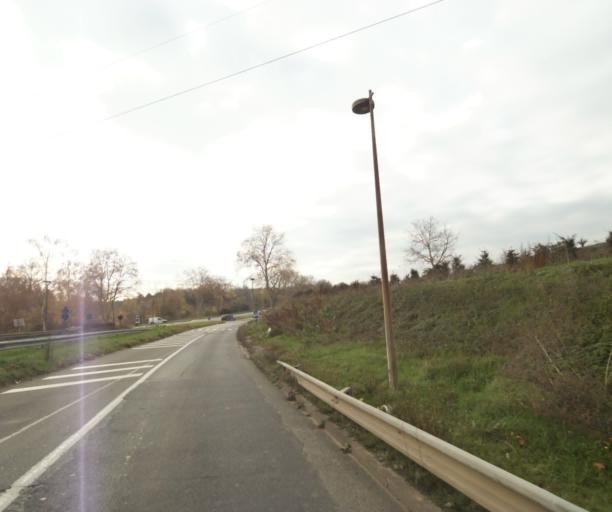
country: FR
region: Ile-de-France
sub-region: Departement du Val-d'Oise
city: Le Thillay
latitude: 48.9992
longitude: 2.4647
